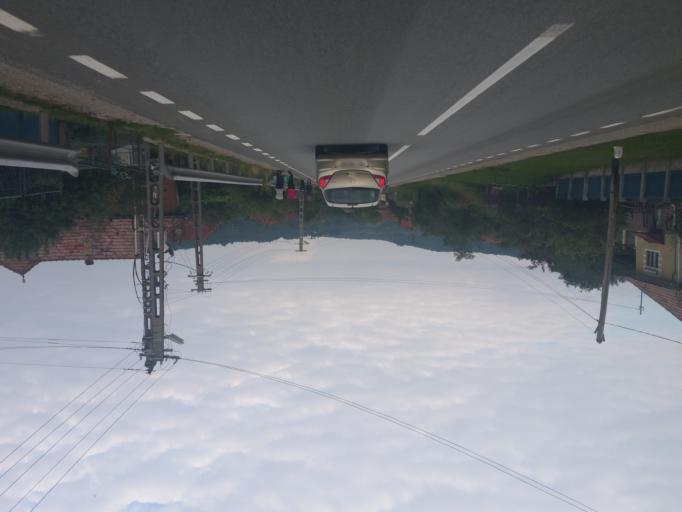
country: RO
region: Salaj
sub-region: Comuna Sanmihaiu Almasului
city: Sanmihaiu Almasului
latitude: 46.9574
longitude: 23.3387
